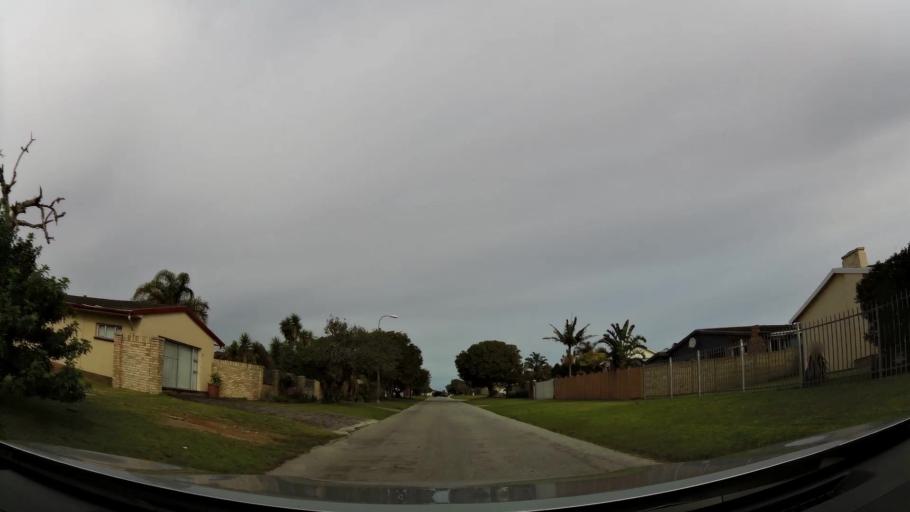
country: ZA
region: Eastern Cape
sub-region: Nelson Mandela Bay Metropolitan Municipality
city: Port Elizabeth
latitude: -33.9374
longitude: 25.4983
